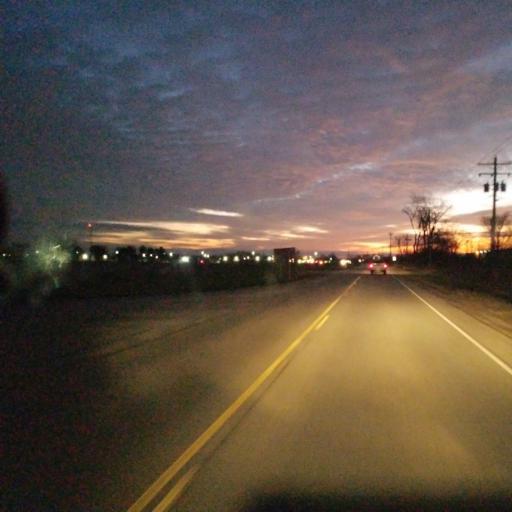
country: US
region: Illinois
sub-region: Peoria County
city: Bellevue
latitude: 40.6895
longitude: -89.7031
